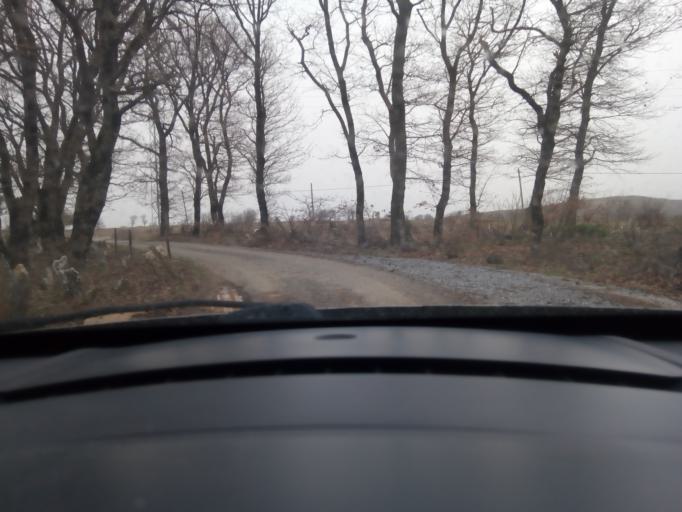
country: TR
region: Balikesir
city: Omerkoy
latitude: 39.8893
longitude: 28.0255
